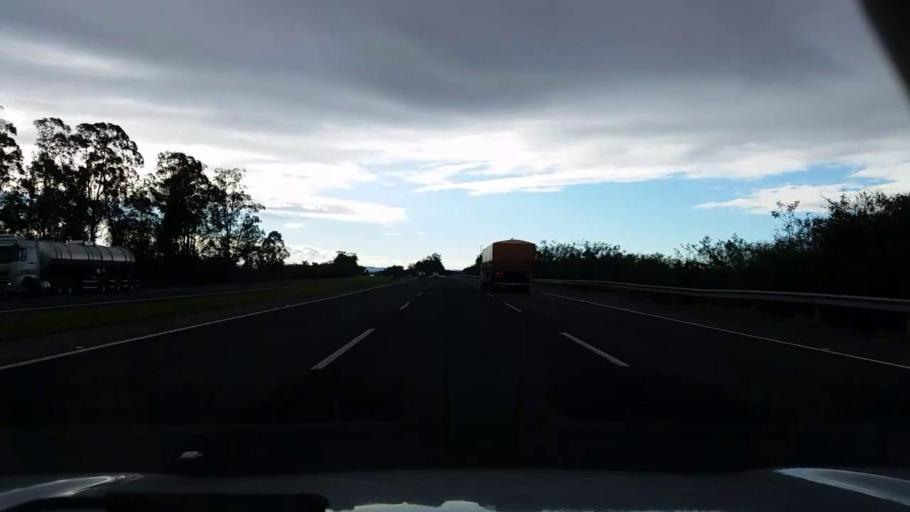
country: BR
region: Rio Grande do Sul
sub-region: Taquara
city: Taquara
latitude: -29.8897
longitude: -50.6857
